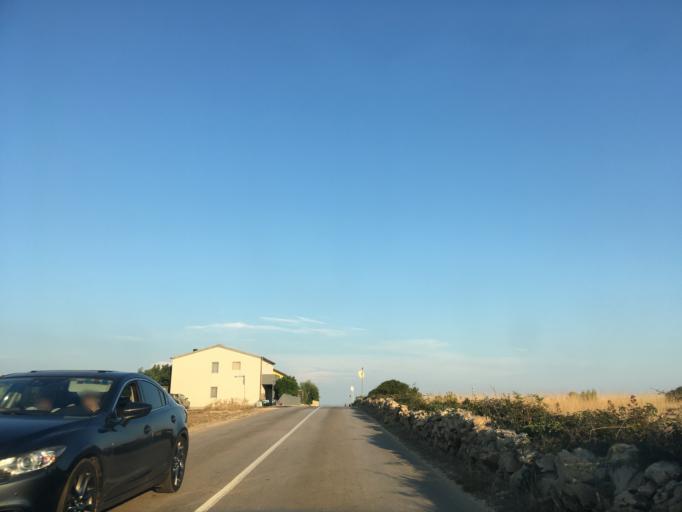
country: HR
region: Zadarska
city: Vir
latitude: 44.2989
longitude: 15.1134
